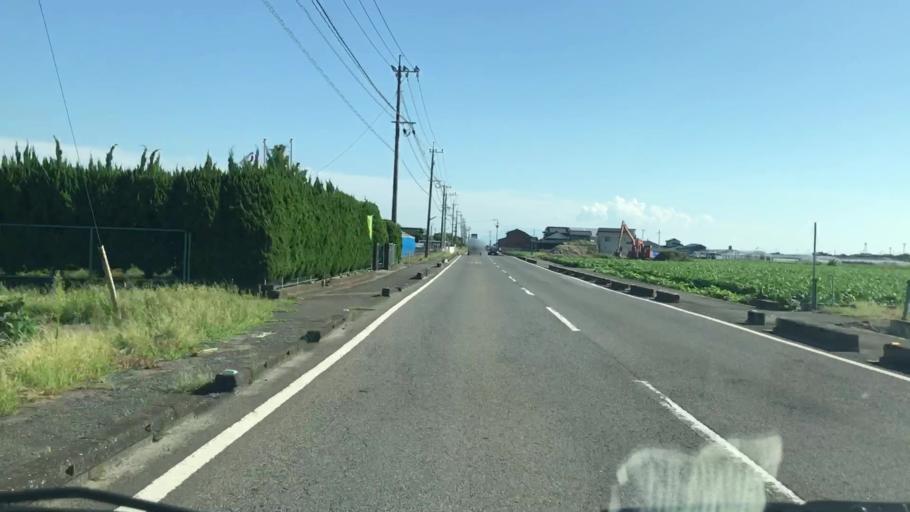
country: JP
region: Saga Prefecture
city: Okawa
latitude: 33.2018
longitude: 130.3352
